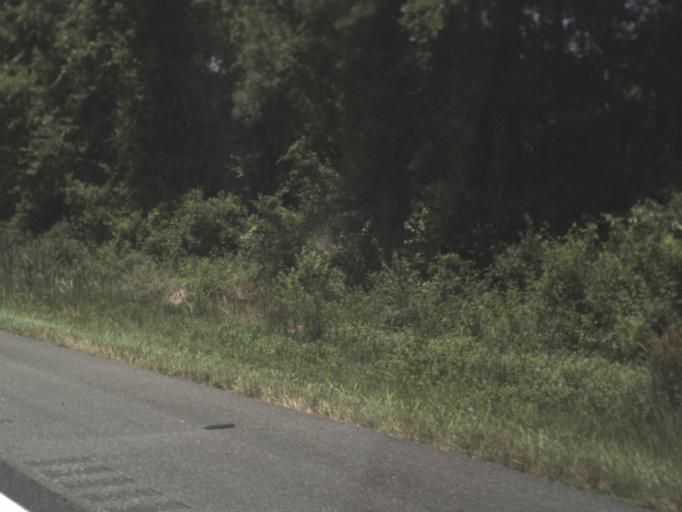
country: US
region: Florida
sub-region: Baker County
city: Macclenny
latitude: 30.2531
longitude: -82.2054
